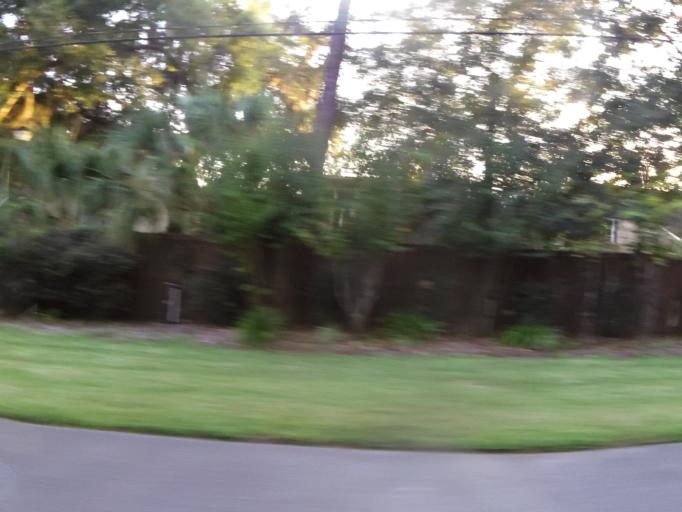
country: US
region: Florida
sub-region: Clay County
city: Orange Park
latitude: 30.1966
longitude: -81.6317
